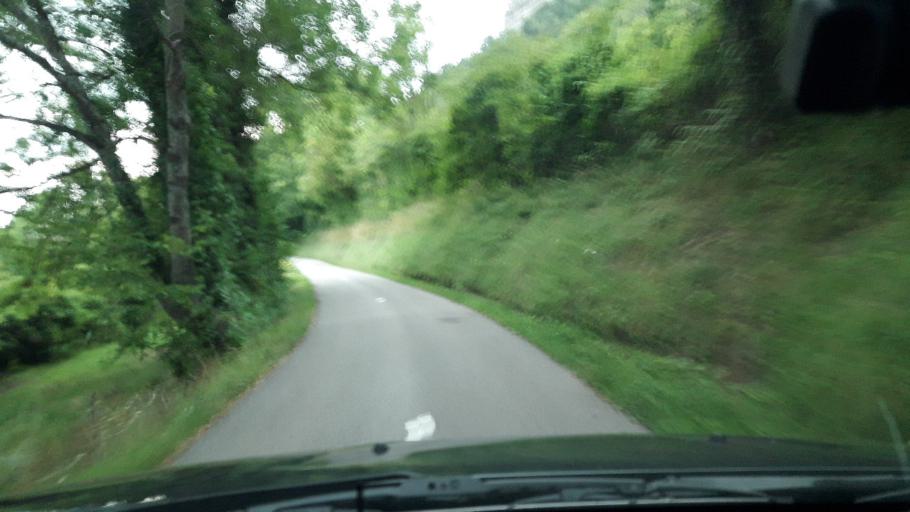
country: FR
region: Rhone-Alpes
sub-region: Departement de la Savoie
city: Barberaz
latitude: 45.5315
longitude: 5.9284
